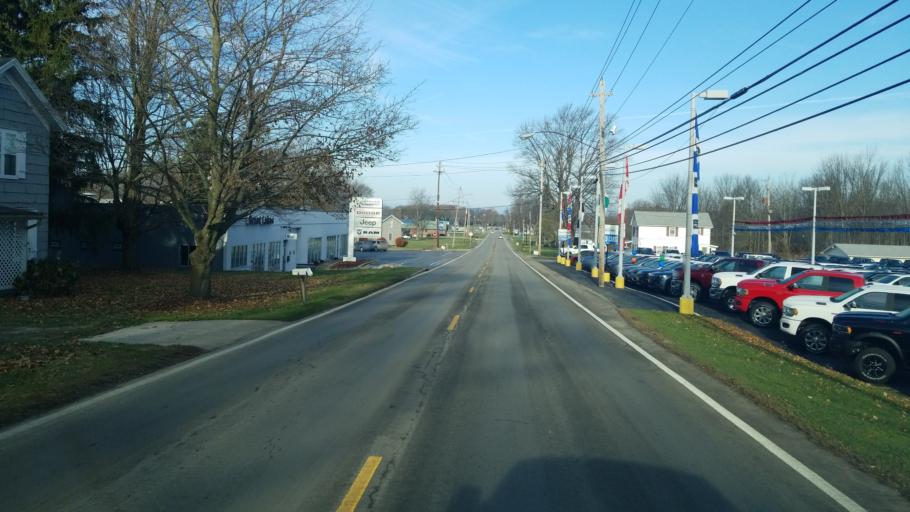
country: US
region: Ohio
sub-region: Ashtabula County
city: North Kingsville
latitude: 41.8932
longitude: -80.6793
